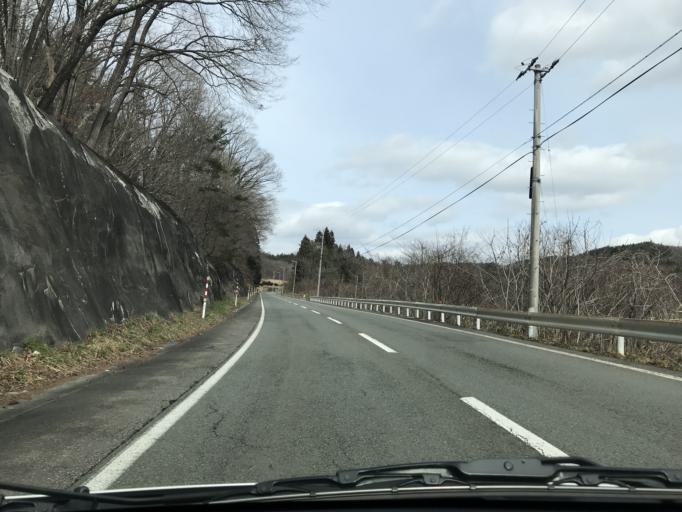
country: JP
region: Iwate
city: Tono
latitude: 39.3061
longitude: 141.3698
